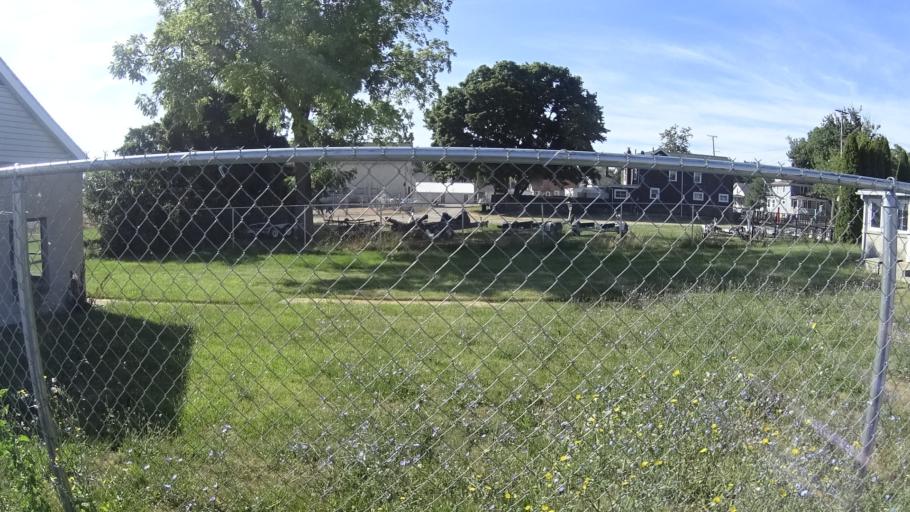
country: US
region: Ohio
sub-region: Erie County
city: Sandusky
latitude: 41.4576
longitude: -82.7008
